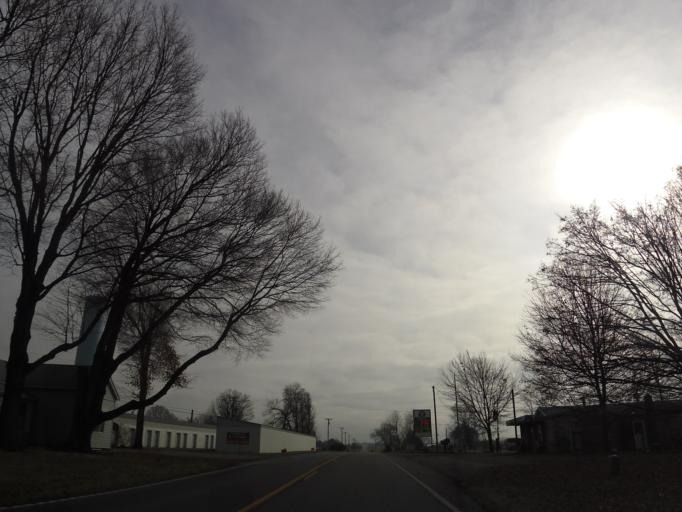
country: US
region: Indiana
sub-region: Jefferson County
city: Madison
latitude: 38.6839
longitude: -85.3276
